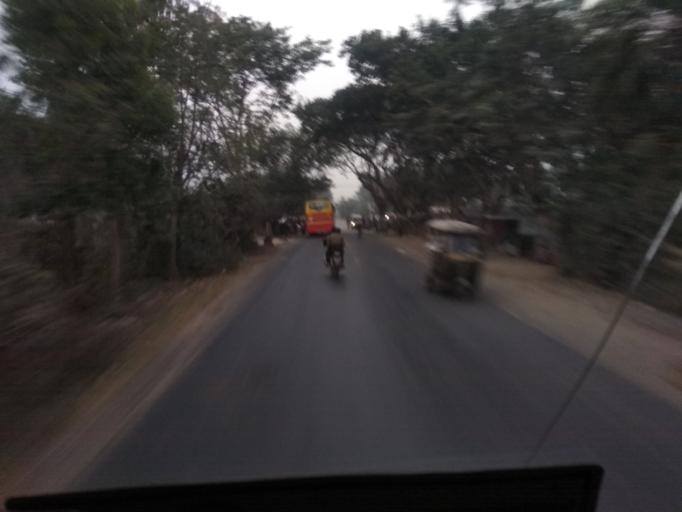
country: BD
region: Rajshahi
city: Bogra
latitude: 24.7362
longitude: 89.3290
